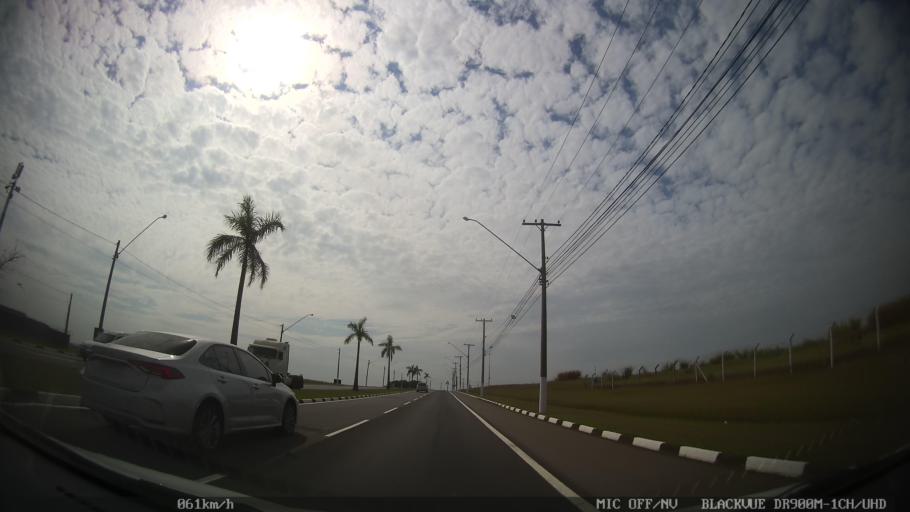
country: BR
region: Sao Paulo
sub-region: Paulinia
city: Paulinia
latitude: -22.7922
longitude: -47.1711
